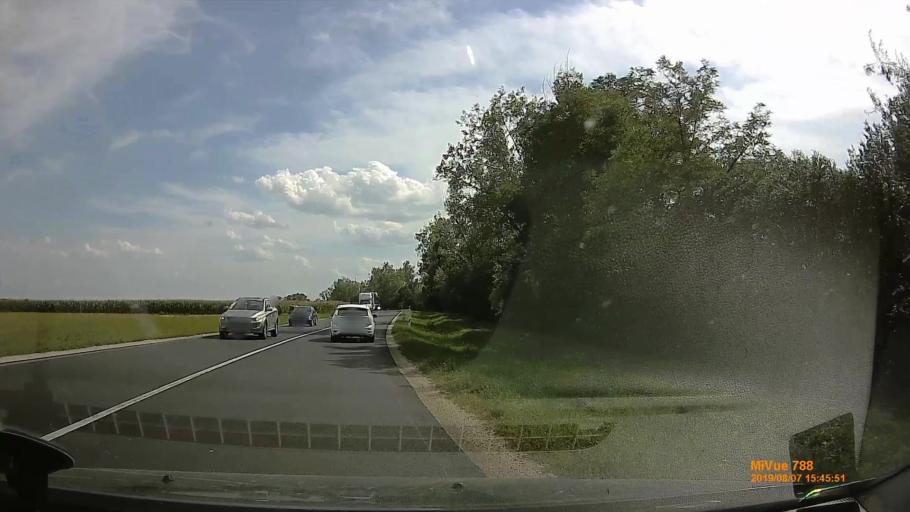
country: HU
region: Vas
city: Szombathely
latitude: 47.1921
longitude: 16.6203
